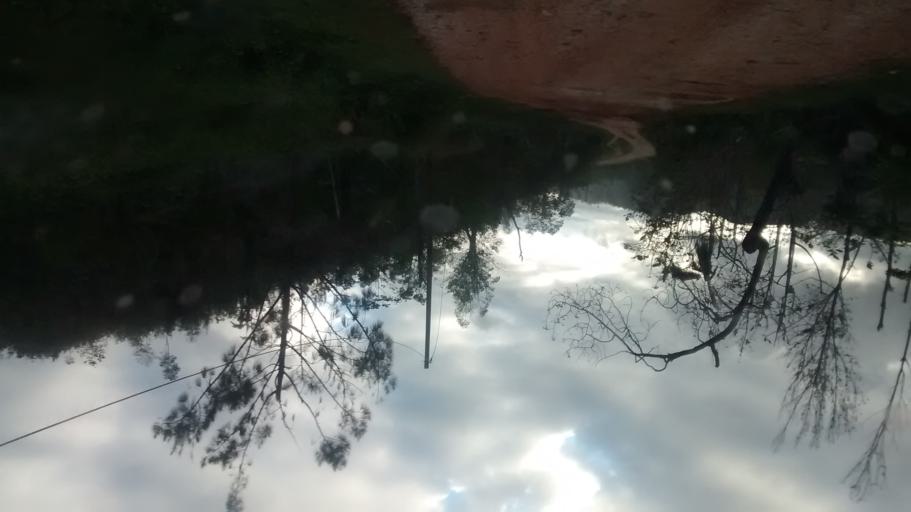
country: HT
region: Grandans
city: Corail
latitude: 18.4795
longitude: -73.8066
